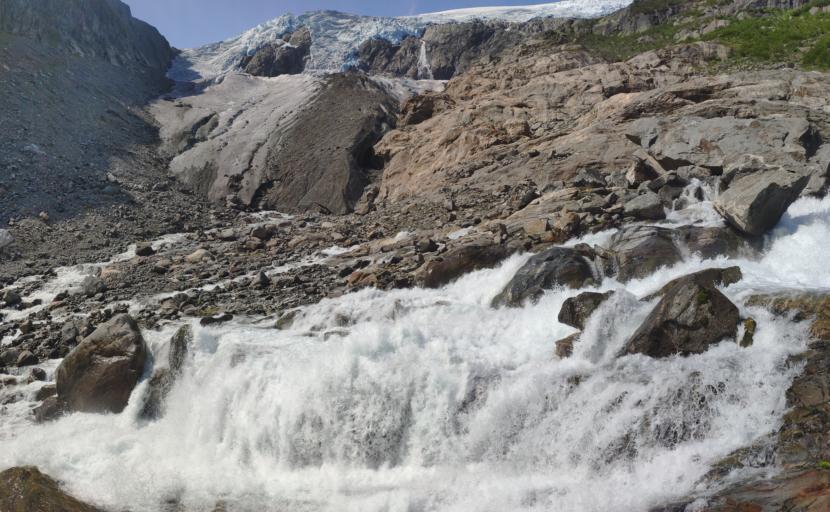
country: NO
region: Hordaland
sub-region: Odda
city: Odda
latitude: 60.0409
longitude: 6.4391
